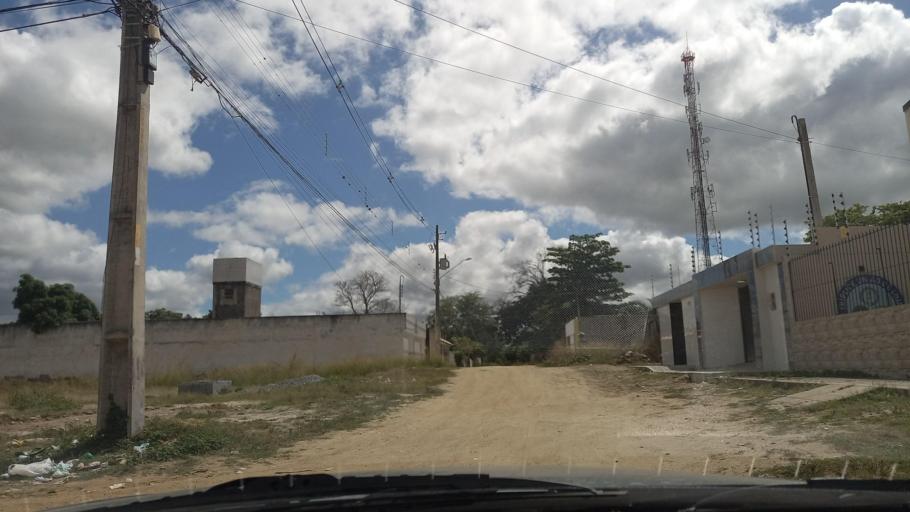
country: BR
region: Pernambuco
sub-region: Caruaru
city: Caruaru
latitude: -8.2547
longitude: -35.9771
